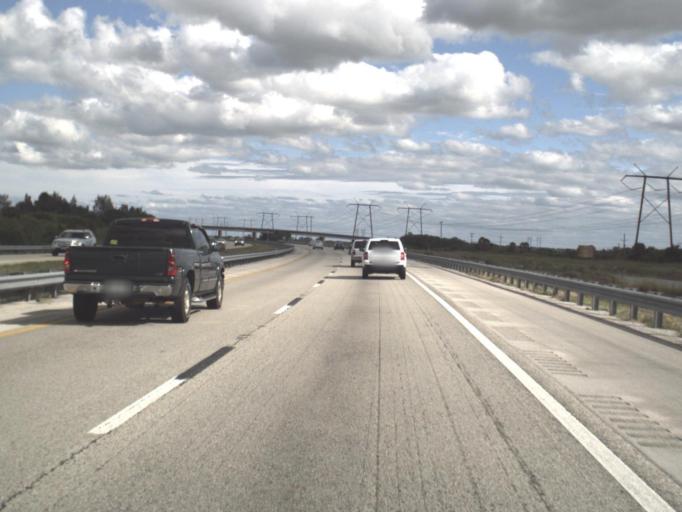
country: US
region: Florida
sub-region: Indian River County
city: West Vero Corridor
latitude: 27.4859
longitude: -80.5644
